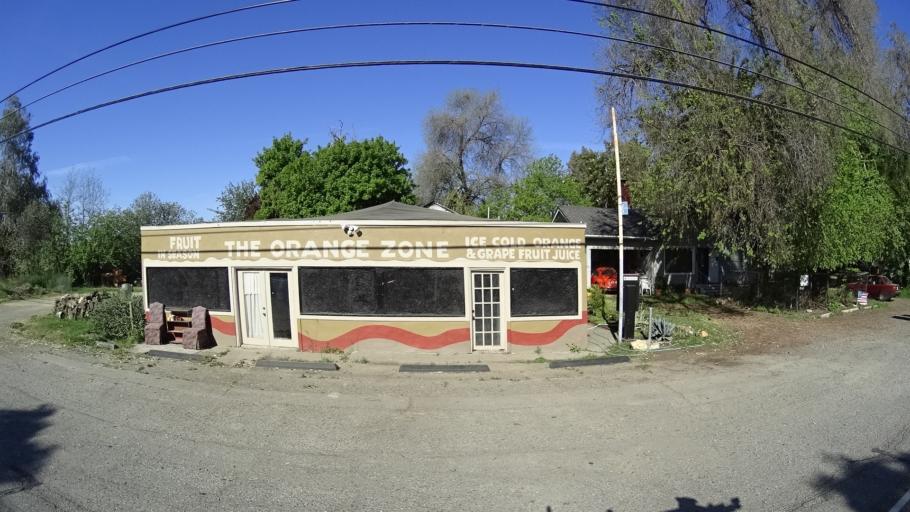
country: US
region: California
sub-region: Glenn County
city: Orland
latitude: 39.7129
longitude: -122.1972
